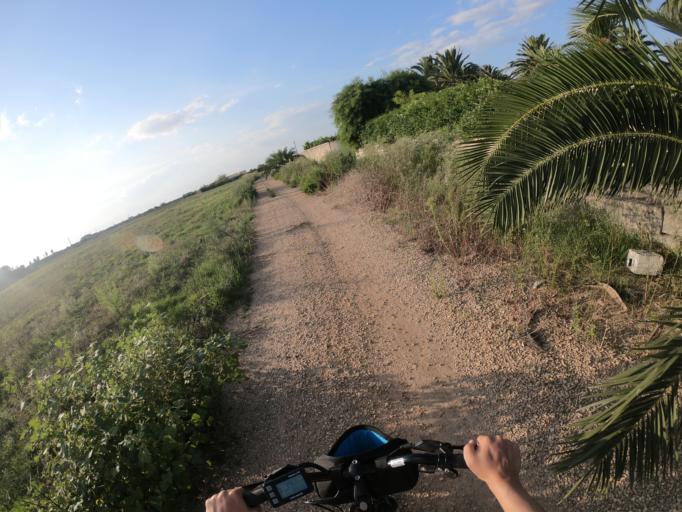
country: IT
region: Apulia
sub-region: Provincia di Lecce
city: Nardo
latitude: 40.1664
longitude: 18.0143
